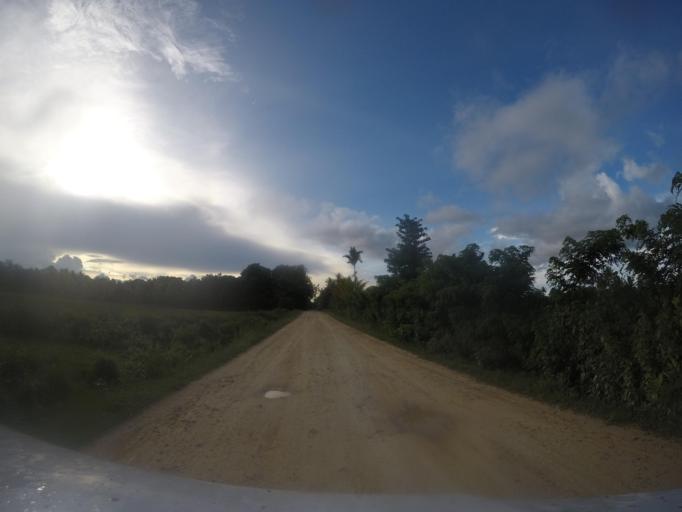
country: TL
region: Lautem
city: Lospalos
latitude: -8.5018
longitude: 127.0037
